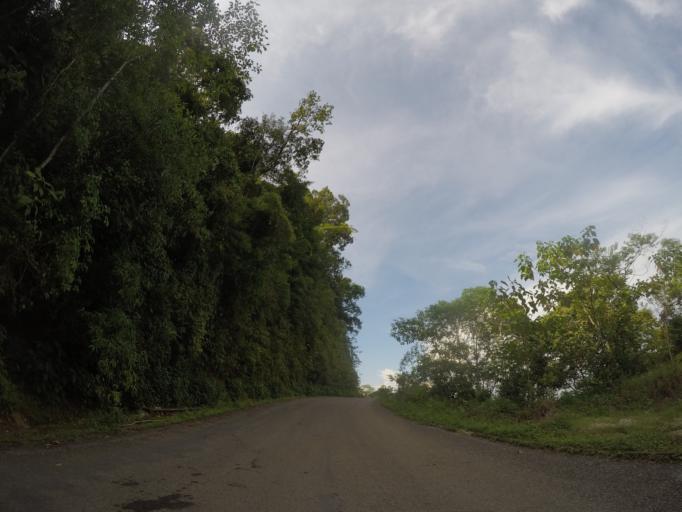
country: MX
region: Oaxaca
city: Pluma Hidalgo
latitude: 15.9372
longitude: -96.4317
